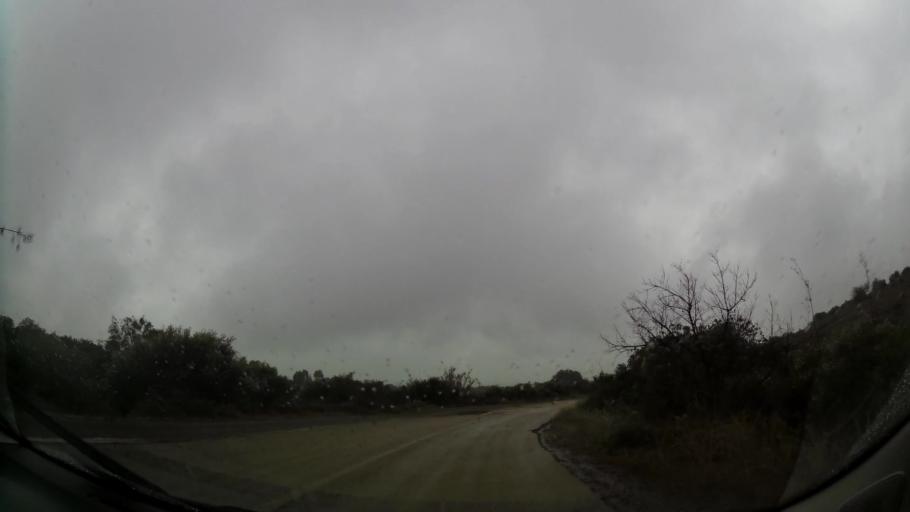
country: MA
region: Taza-Al Hoceima-Taounate
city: Imzourene
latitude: 35.1177
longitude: -3.7790
